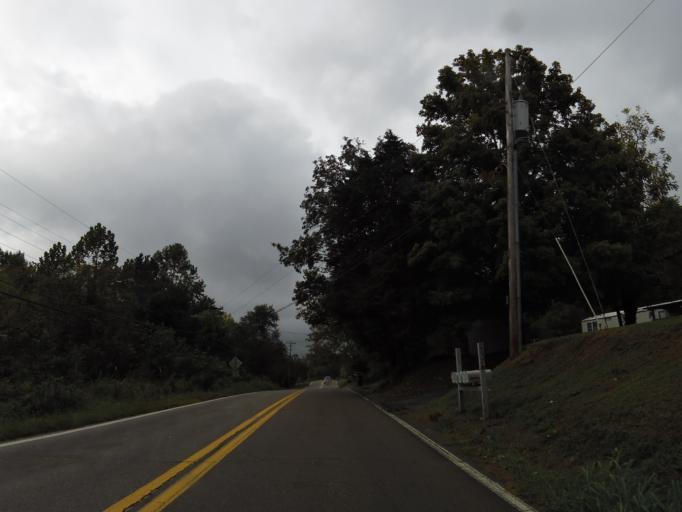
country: US
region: Tennessee
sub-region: Bradley County
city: Cleveland
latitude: 35.1805
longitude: -84.9281
